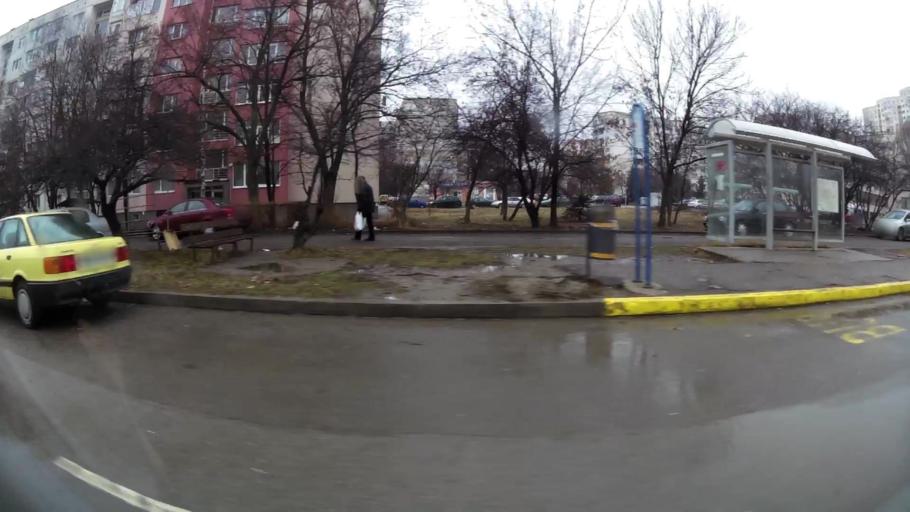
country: BG
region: Sofia-Capital
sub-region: Stolichna Obshtina
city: Sofia
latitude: 42.6411
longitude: 23.3837
